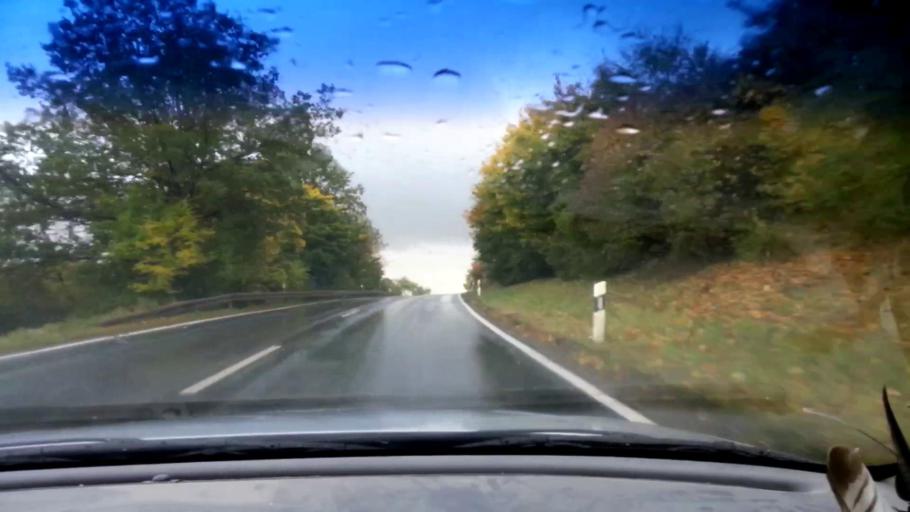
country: DE
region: Bavaria
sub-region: Upper Franconia
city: Burgebrach
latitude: 49.8407
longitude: 10.7340
